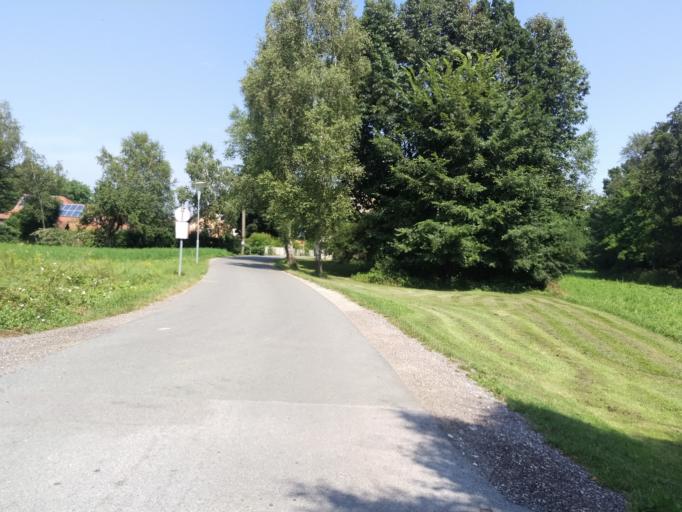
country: AT
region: Styria
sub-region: Politischer Bezirk Graz-Umgebung
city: Gossendorf
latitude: 46.9873
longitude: 15.4696
